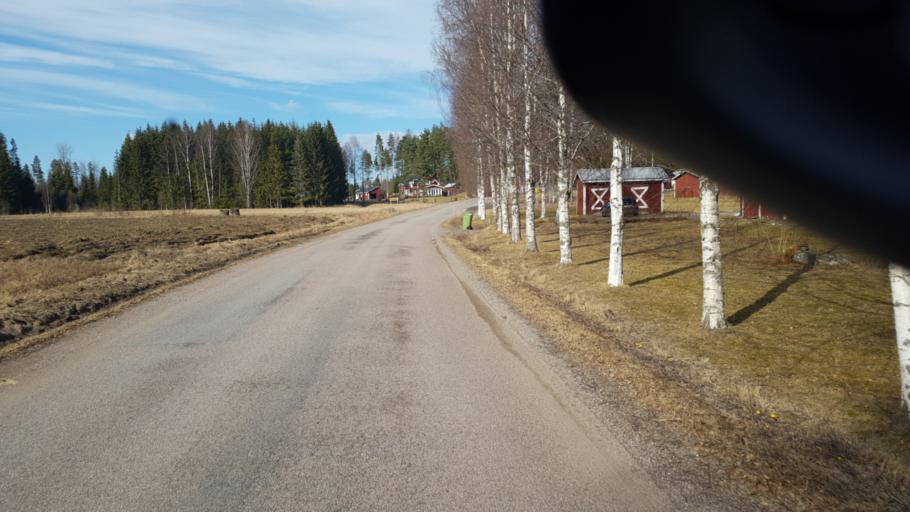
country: SE
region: Vaermland
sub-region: Eda Kommun
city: Charlottenberg
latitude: 59.8608
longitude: 12.3439
